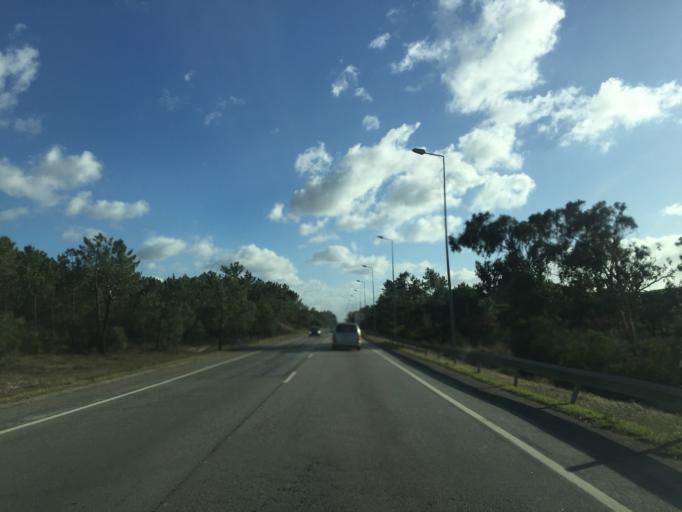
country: PT
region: Coimbra
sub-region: Figueira da Foz
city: Lavos
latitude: 40.0968
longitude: -8.8547
